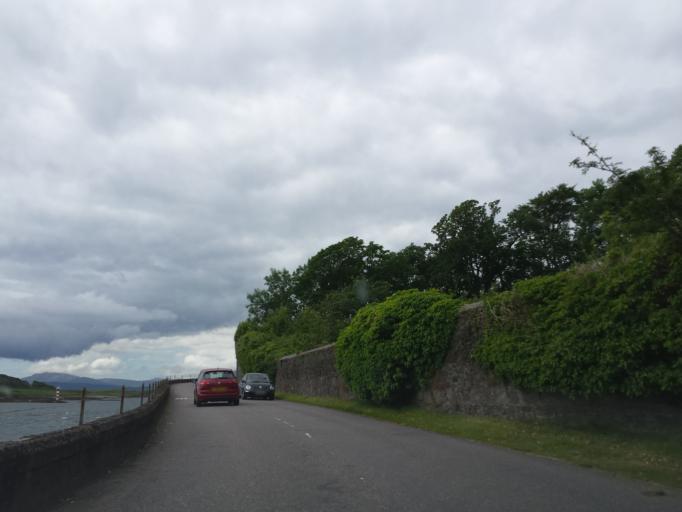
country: GB
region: Scotland
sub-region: Argyll and Bute
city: Oban
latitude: 56.4258
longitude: -5.4843
